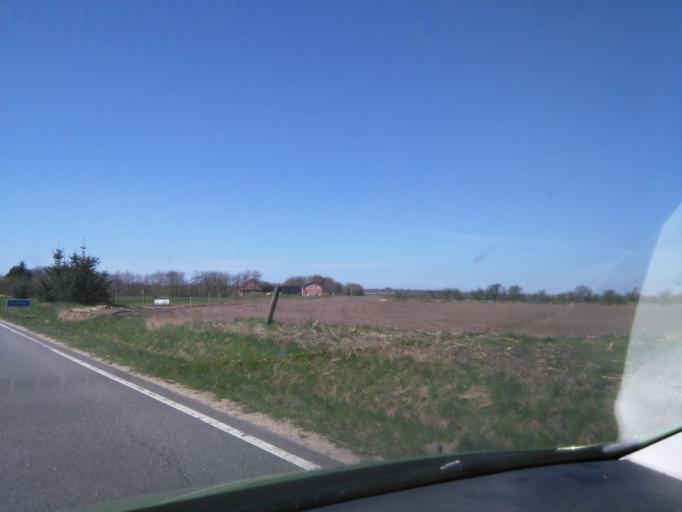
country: DK
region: South Denmark
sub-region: Varde Kommune
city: Varde
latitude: 55.6273
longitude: 8.4048
